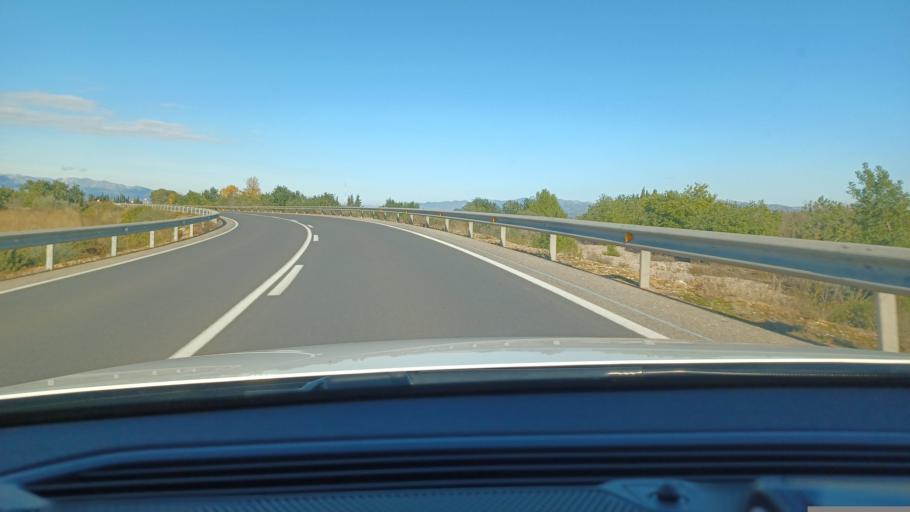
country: ES
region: Catalonia
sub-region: Provincia de Tarragona
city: Santa Barbara
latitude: 40.7189
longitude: 0.5057
